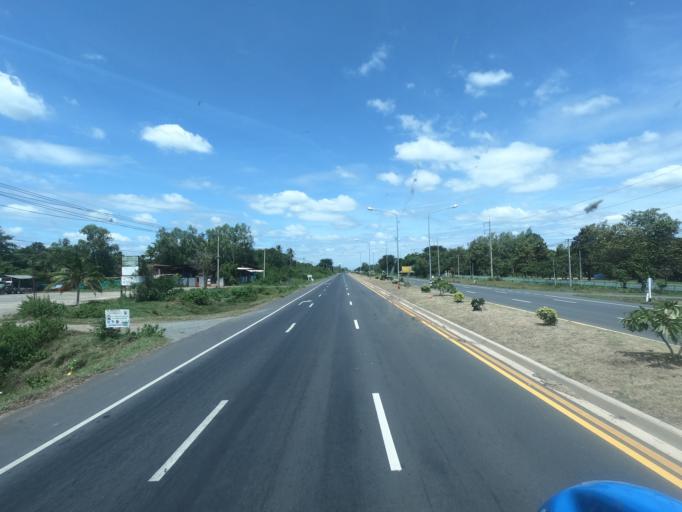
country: TH
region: Surin
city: Prasat
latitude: 14.6268
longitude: 103.3938
